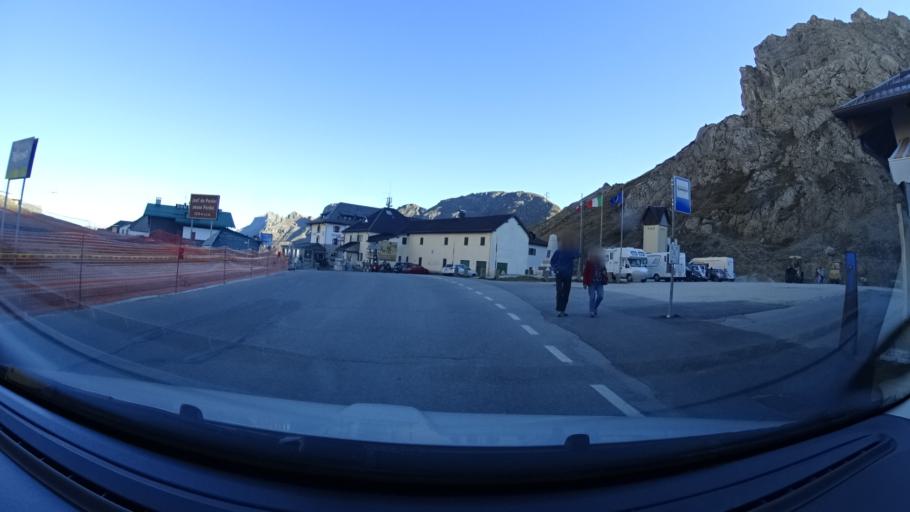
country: IT
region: Trentino-Alto Adige
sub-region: Provincia di Trento
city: Canazei
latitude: 46.4877
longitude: 11.8119
